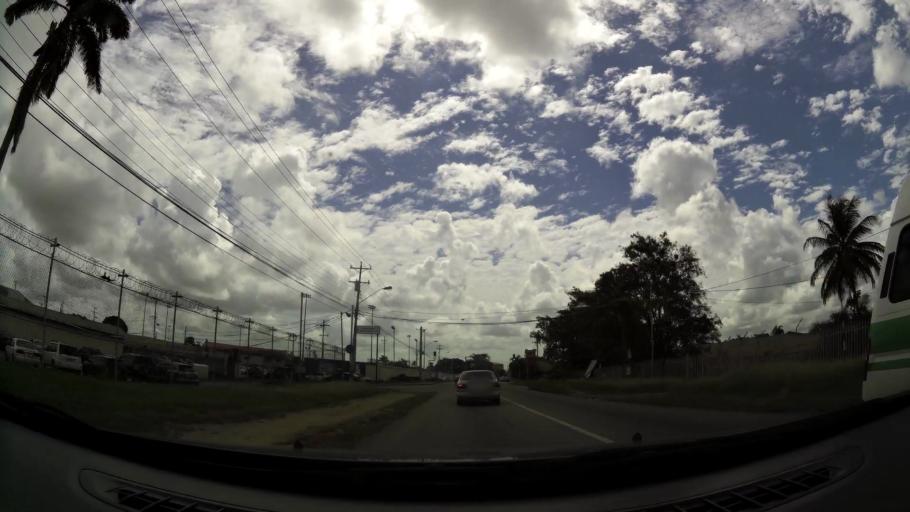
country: TT
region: City of San Fernando
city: Marabella
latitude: 10.3120
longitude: -61.4529
